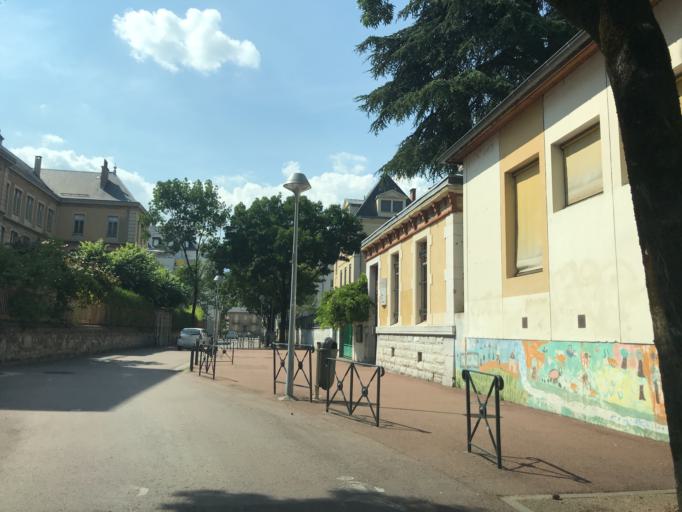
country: FR
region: Rhone-Alpes
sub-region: Departement de la Savoie
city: Jacob-Bellecombette
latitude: 45.5681
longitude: 5.9159
